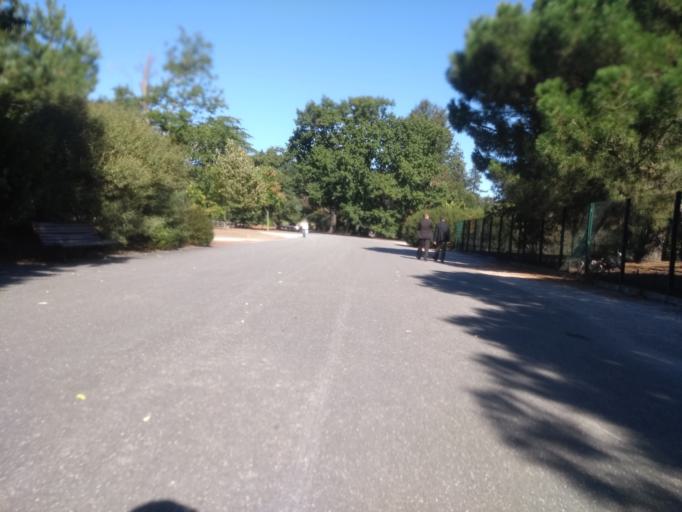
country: FR
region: Aquitaine
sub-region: Departement de la Gironde
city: Le Bouscat
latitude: 44.8523
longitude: -0.6047
